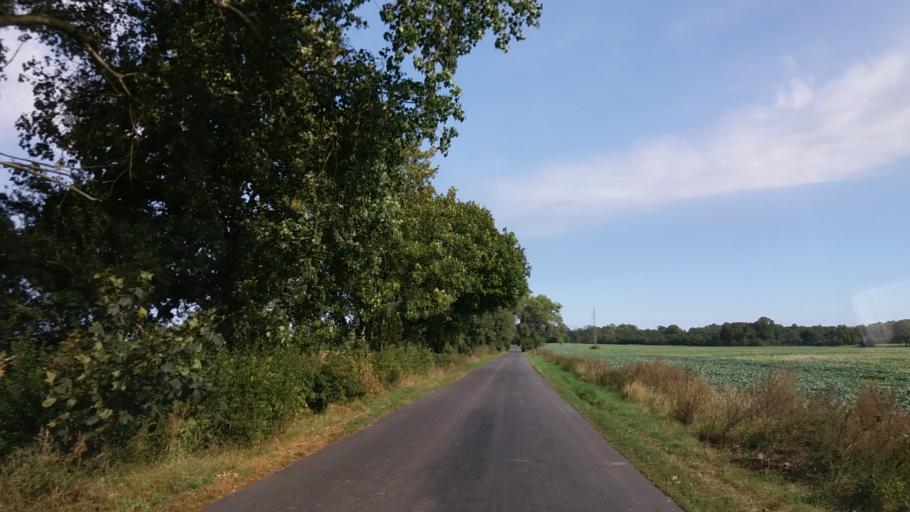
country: PL
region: West Pomeranian Voivodeship
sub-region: Powiat stargardzki
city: Suchan
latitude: 53.2160
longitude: 15.3400
